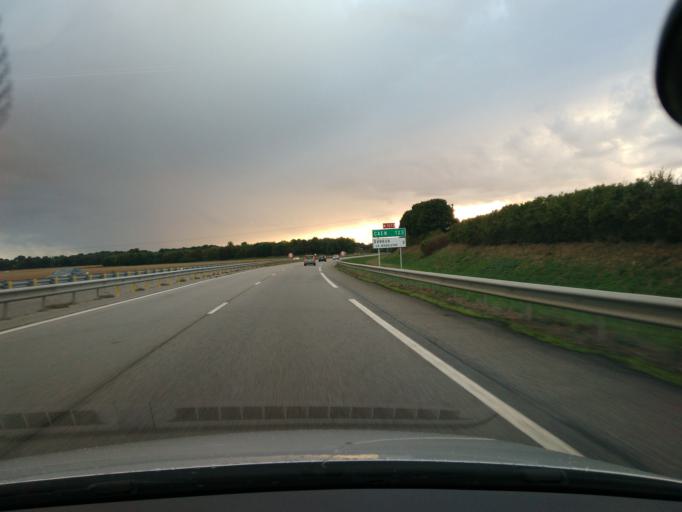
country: FR
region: Haute-Normandie
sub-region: Departement de l'Eure
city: Evreux
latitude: 49.0005
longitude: 1.1833
